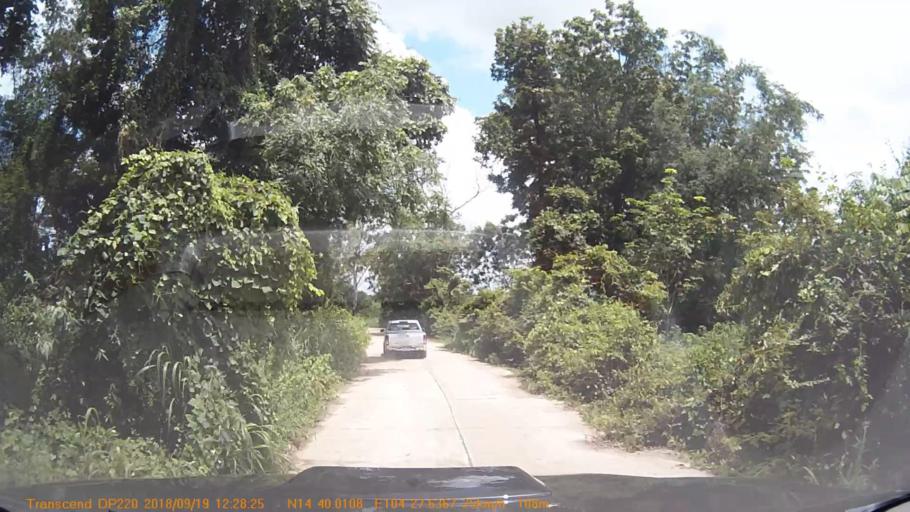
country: TH
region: Sisaket
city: Khun Han
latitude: 14.6671
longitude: 104.4611
